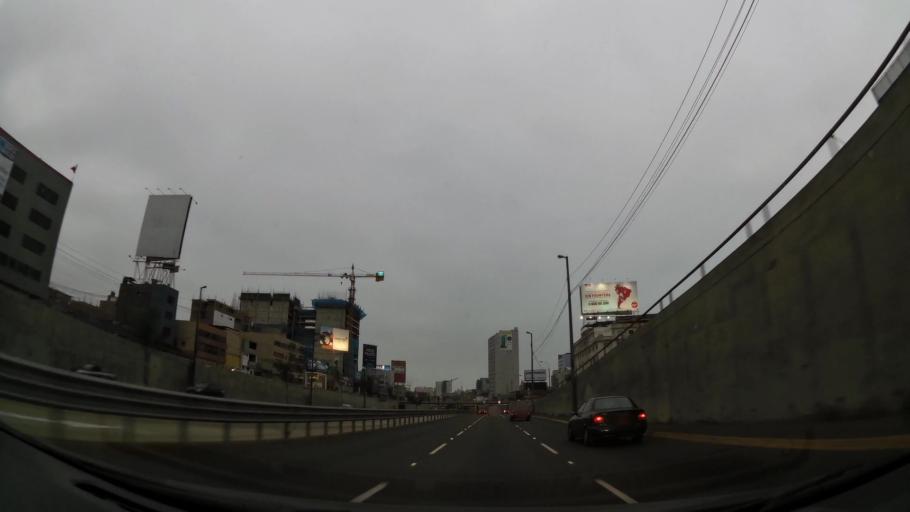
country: PE
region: Lima
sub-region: Lima
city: San Isidro
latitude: -12.1149
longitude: -77.0262
